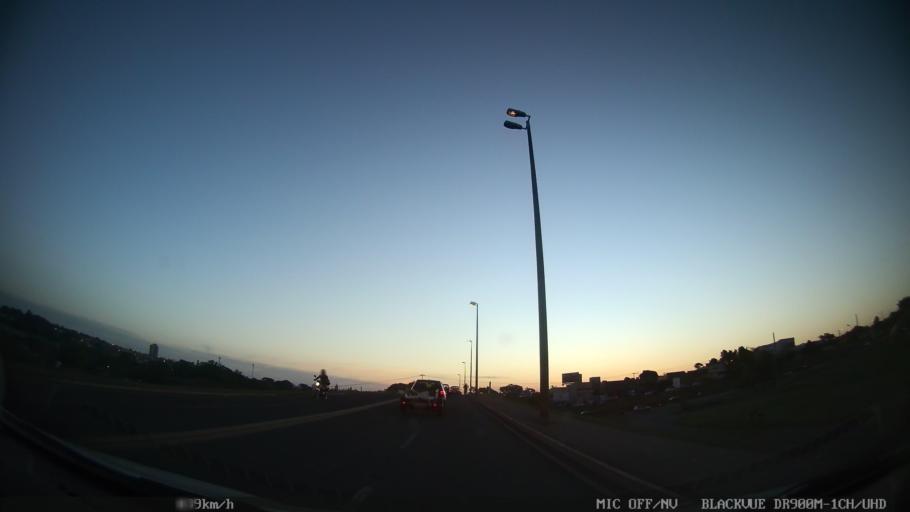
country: BR
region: Sao Paulo
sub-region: Sao Jose Do Rio Preto
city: Sao Jose do Rio Preto
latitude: -20.8090
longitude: -49.3559
